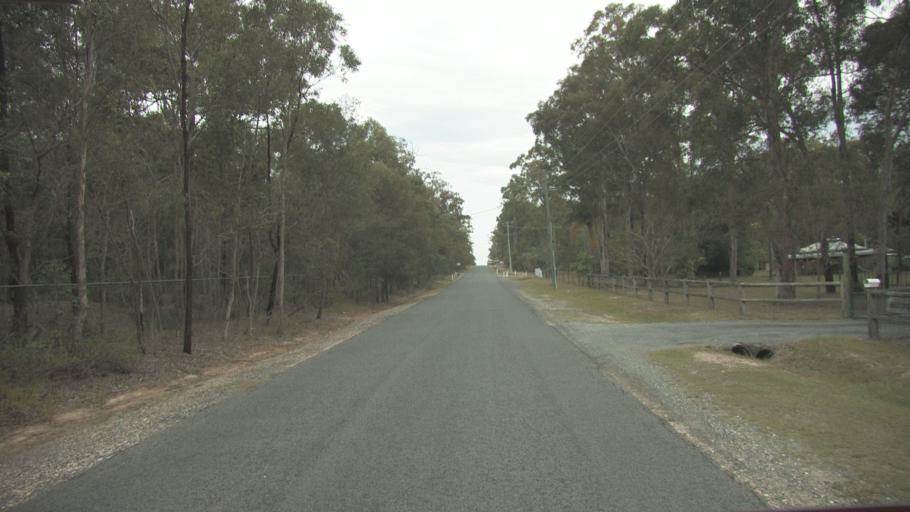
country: AU
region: Queensland
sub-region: Logan
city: Chambers Flat
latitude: -27.7932
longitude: 153.1214
